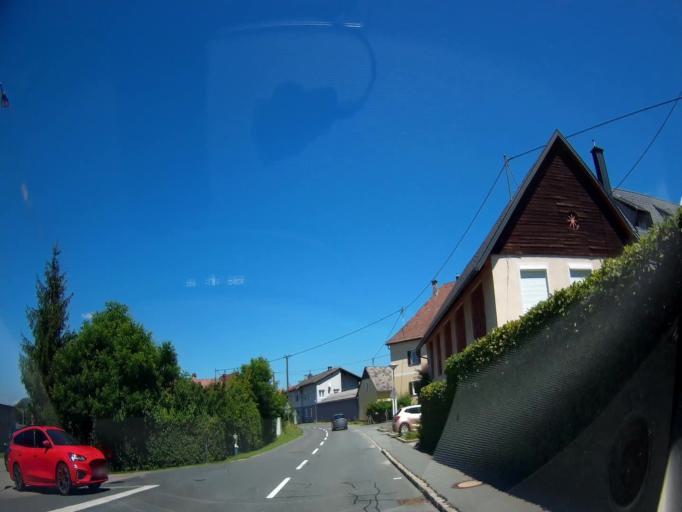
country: AT
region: Carinthia
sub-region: Politischer Bezirk Klagenfurt Land
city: Ferlach
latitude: 46.5221
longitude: 14.2981
